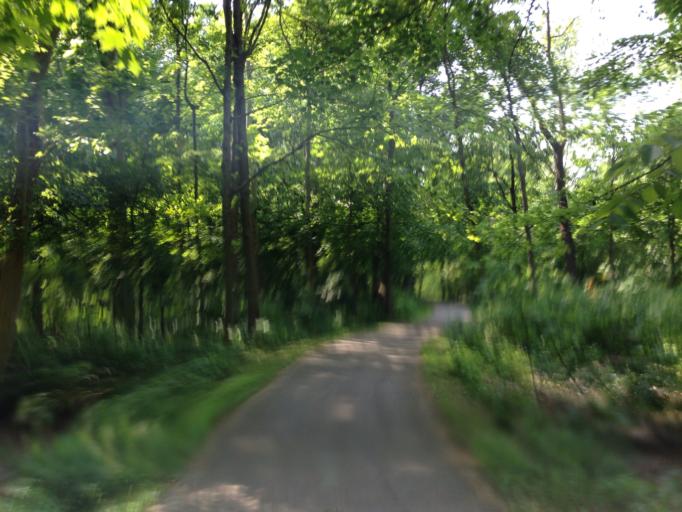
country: US
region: Ohio
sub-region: Cuyahoga County
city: Berea
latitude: 41.3905
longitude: -81.8761
